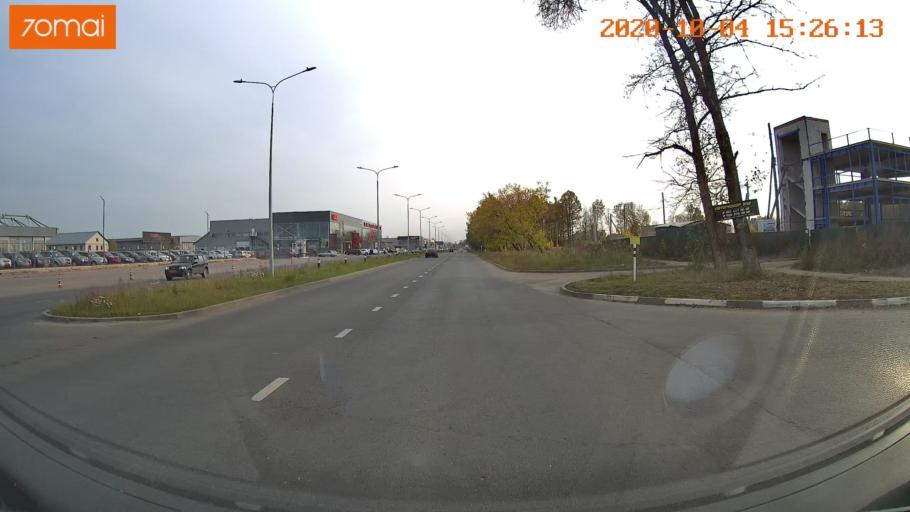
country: RU
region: Ivanovo
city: Bogorodskoye
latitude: 57.0483
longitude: 40.9658
